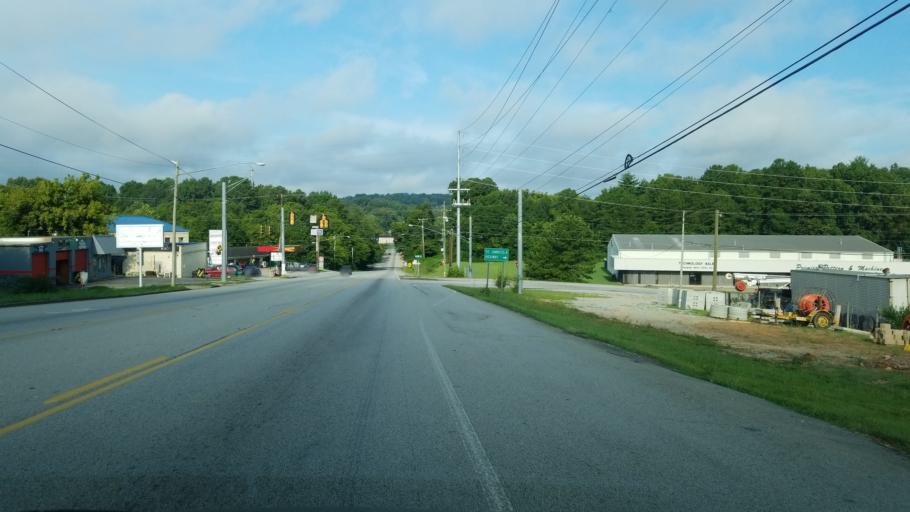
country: US
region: Tennessee
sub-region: Hamilton County
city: East Chattanooga
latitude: 35.0811
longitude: -85.2130
